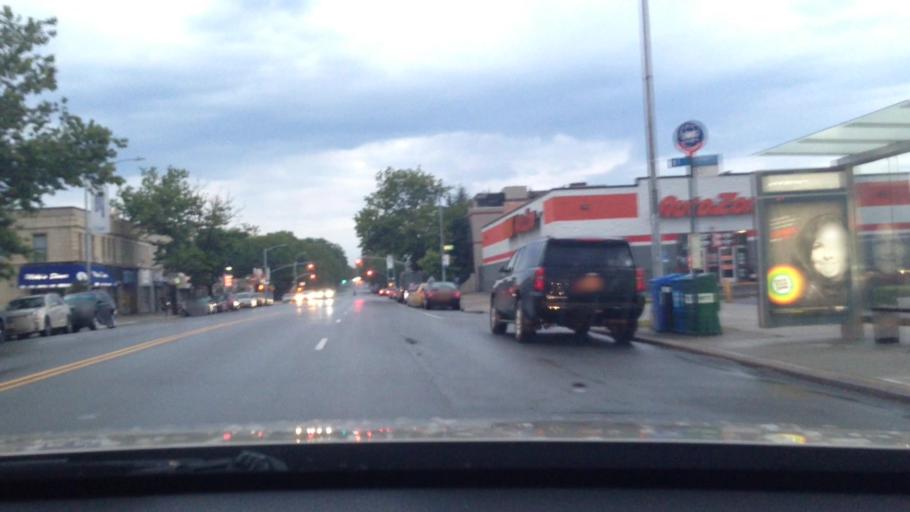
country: US
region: New York
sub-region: Kings County
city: Bensonhurst
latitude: 40.6115
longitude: -74.0097
